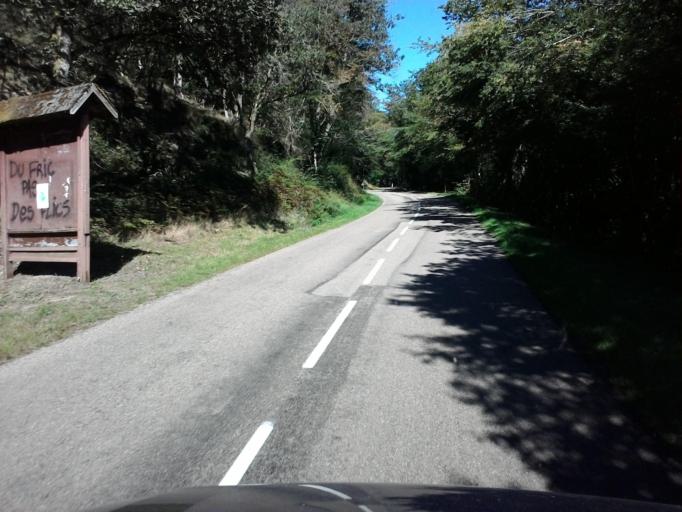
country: FR
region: Bourgogne
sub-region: Departement de la Nievre
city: Lormes
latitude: 47.2163
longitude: 3.9332
